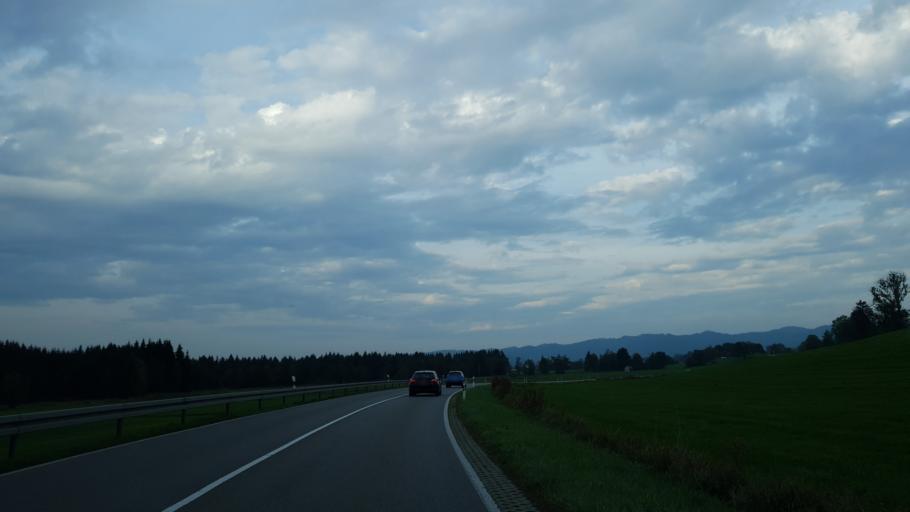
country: DE
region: Bavaria
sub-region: Swabia
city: Gestratz
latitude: 47.6828
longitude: 10.0002
